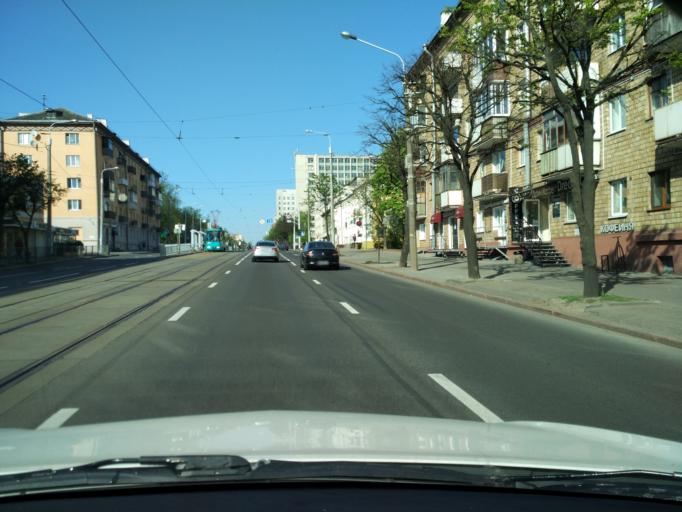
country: BY
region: Minsk
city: Minsk
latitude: 53.9191
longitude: 27.5865
